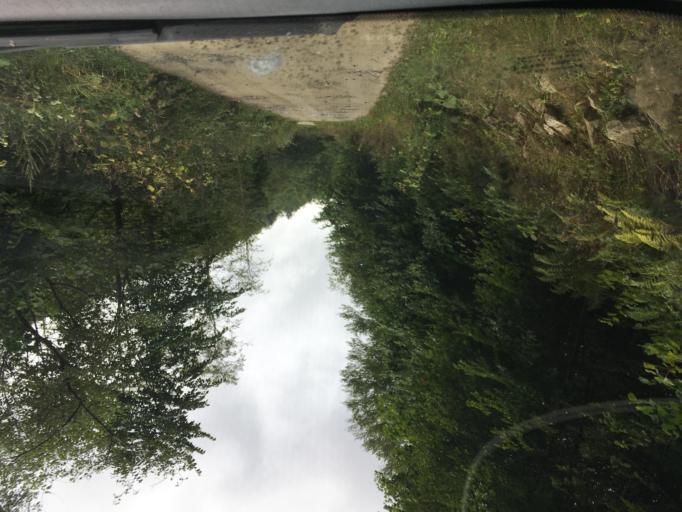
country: PL
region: Subcarpathian Voivodeship
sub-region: Powiat bieszczadzki
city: Lutowiska
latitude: 49.1789
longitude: 22.6189
